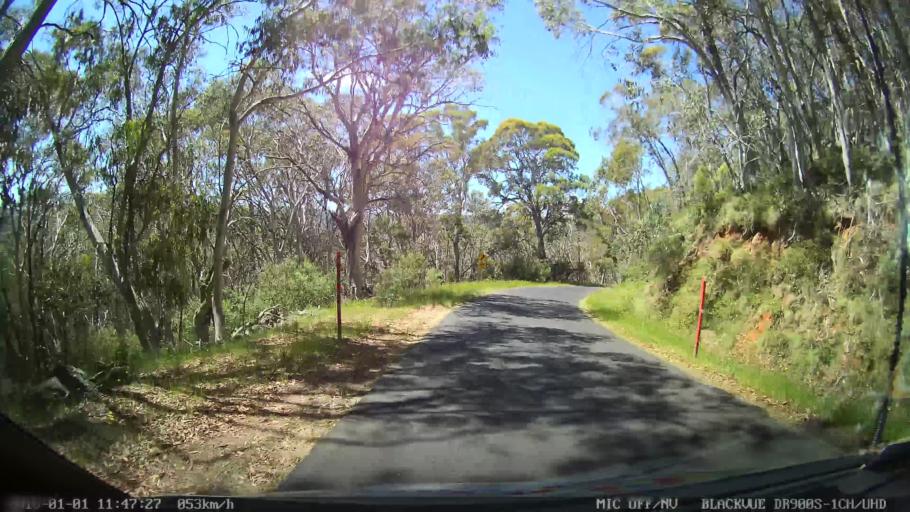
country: AU
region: New South Wales
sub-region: Snowy River
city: Jindabyne
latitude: -35.8914
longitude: 148.4043
